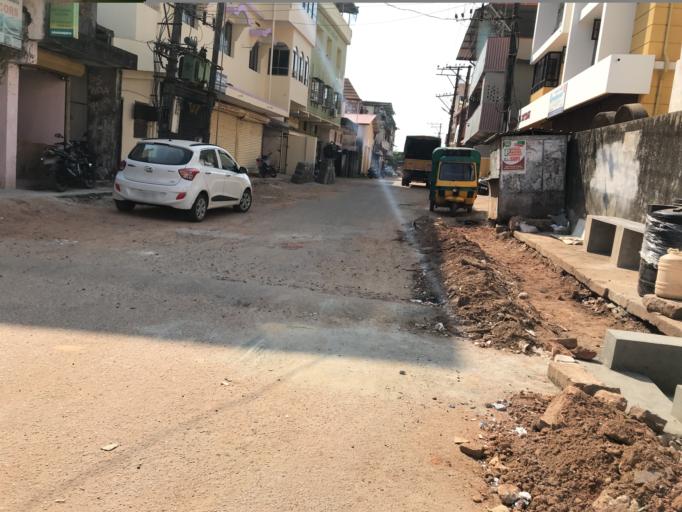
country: IN
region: Karnataka
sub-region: Dakshina Kannada
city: Mangalore
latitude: 12.8695
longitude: 74.8324
